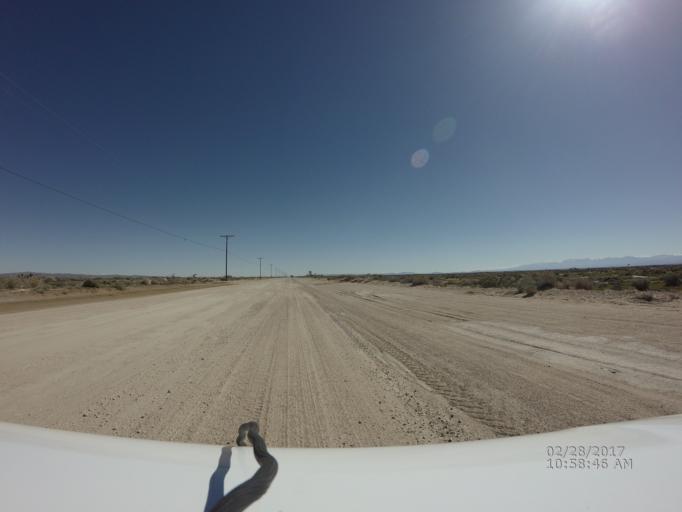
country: US
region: California
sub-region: Kern County
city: Rosamond
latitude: 34.8058
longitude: -118.1942
